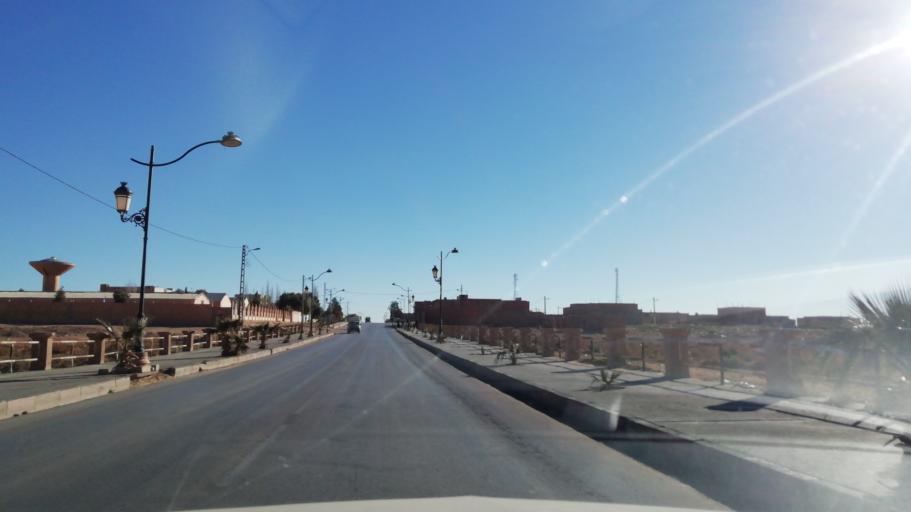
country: DZ
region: El Bayadh
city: El Bayadh
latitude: 33.8527
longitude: 0.6394
